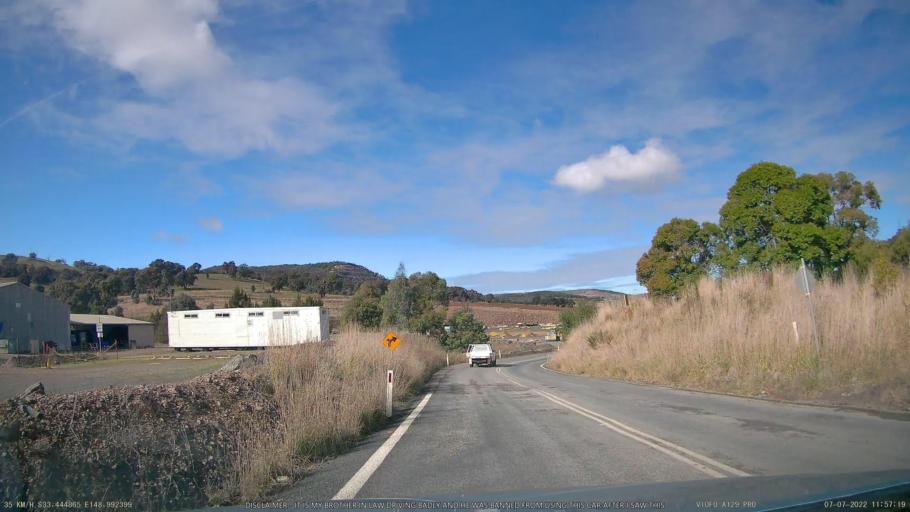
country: AU
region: New South Wales
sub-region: Blayney
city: Millthorpe
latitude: -33.4451
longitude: 148.9929
